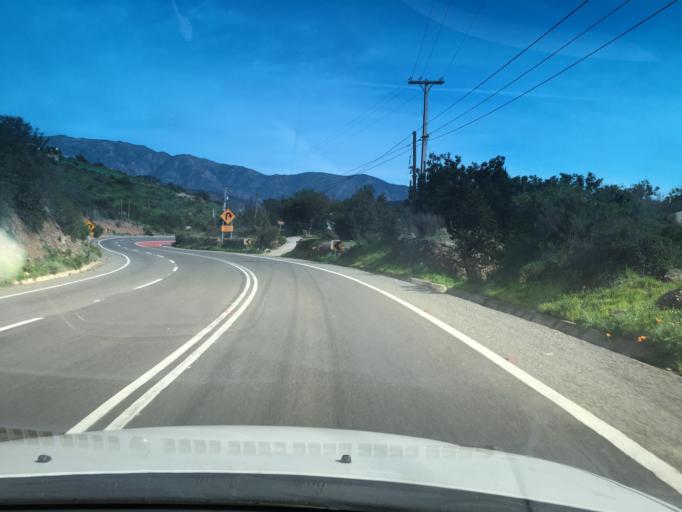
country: CL
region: Valparaiso
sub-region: Provincia de Marga Marga
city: Limache
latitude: -33.0597
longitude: -71.0392
